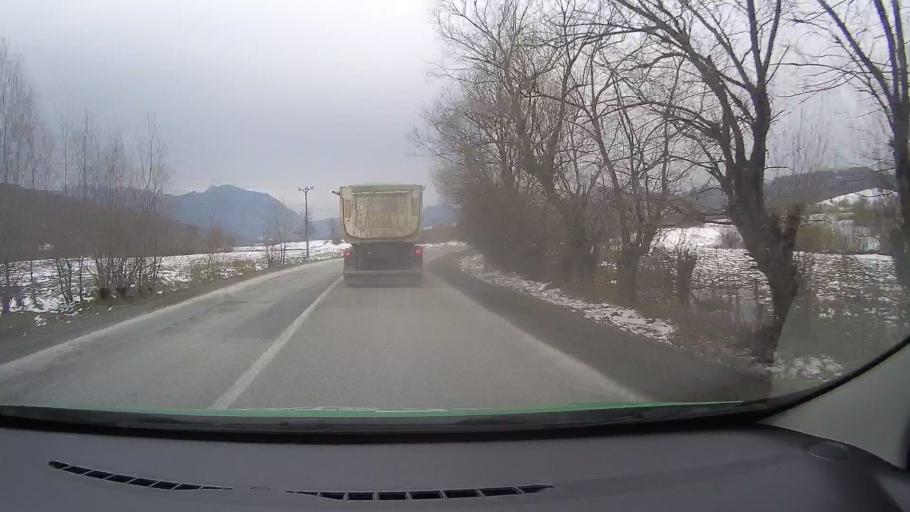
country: RO
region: Brasov
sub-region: Oras Rasnov
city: Rasnov
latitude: 45.5619
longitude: 25.4627
